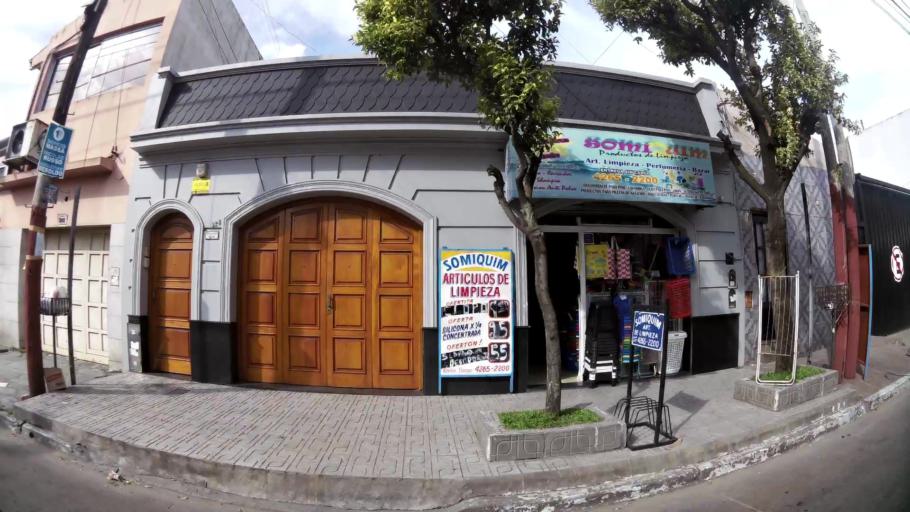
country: AR
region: Buenos Aires
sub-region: Partido de Lanus
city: Lanus
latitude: -34.6919
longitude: -58.3766
